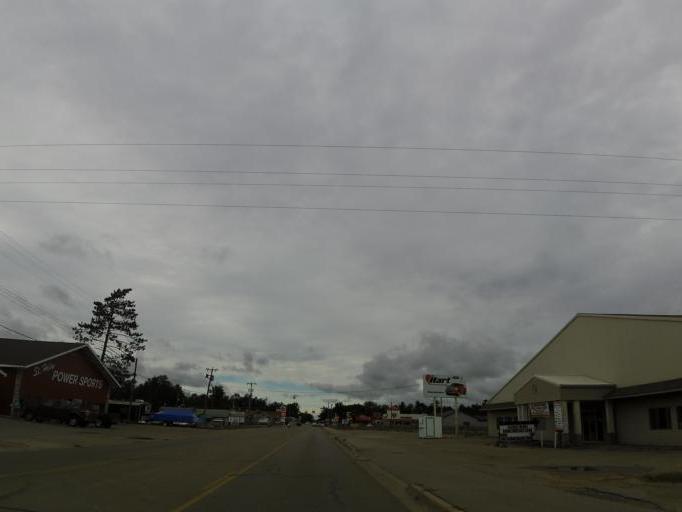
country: US
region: Michigan
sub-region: Roscommon County
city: Saint Helen
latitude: 44.3616
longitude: -84.4102
